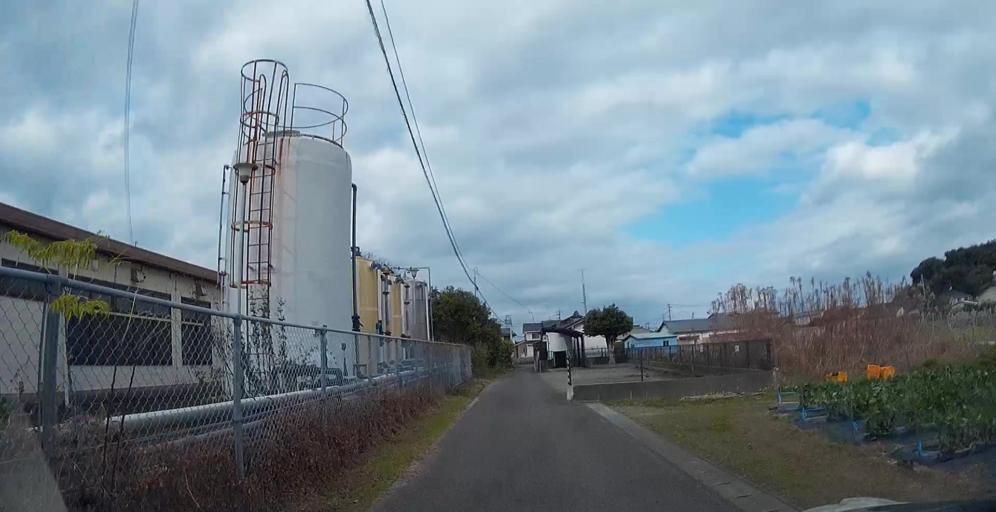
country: JP
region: Kumamoto
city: Minamata
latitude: 32.2104
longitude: 130.3878
